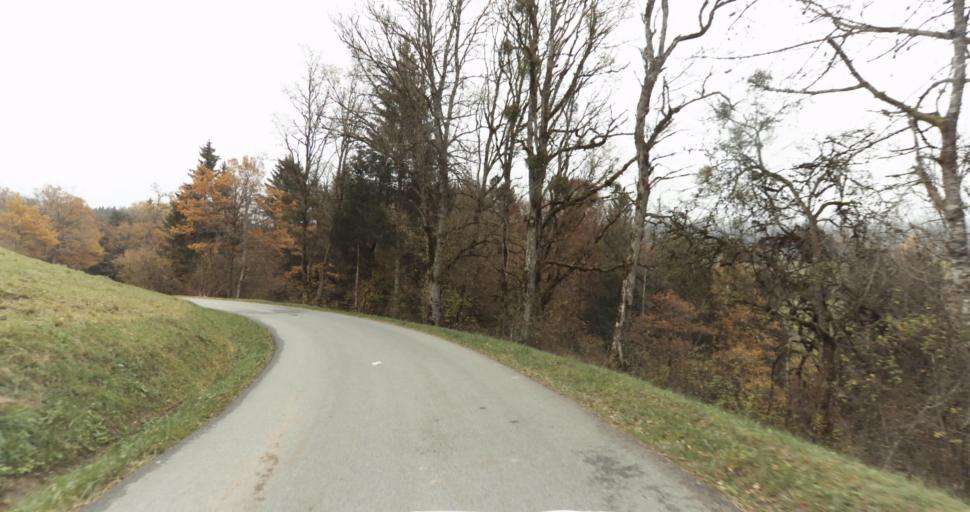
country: FR
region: Rhone-Alpes
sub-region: Departement de la Haute-Savoie
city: Saint-Jorioz
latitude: 45.7556
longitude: 6.1338
